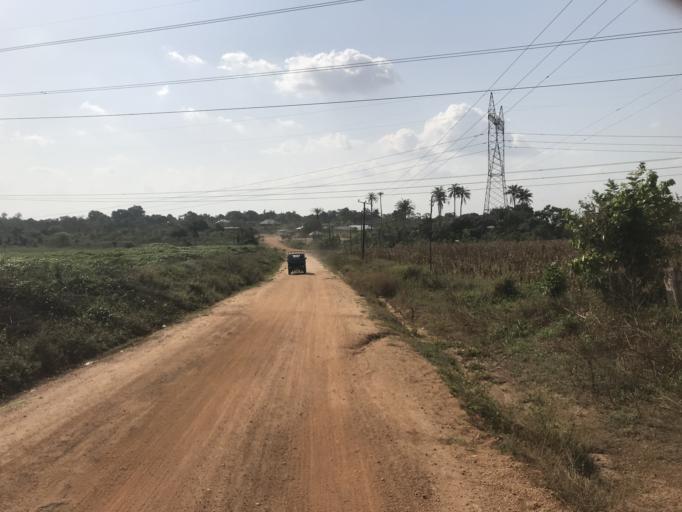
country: NG
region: Osun
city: Osogbo
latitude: 7.8433
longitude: 4.5767
